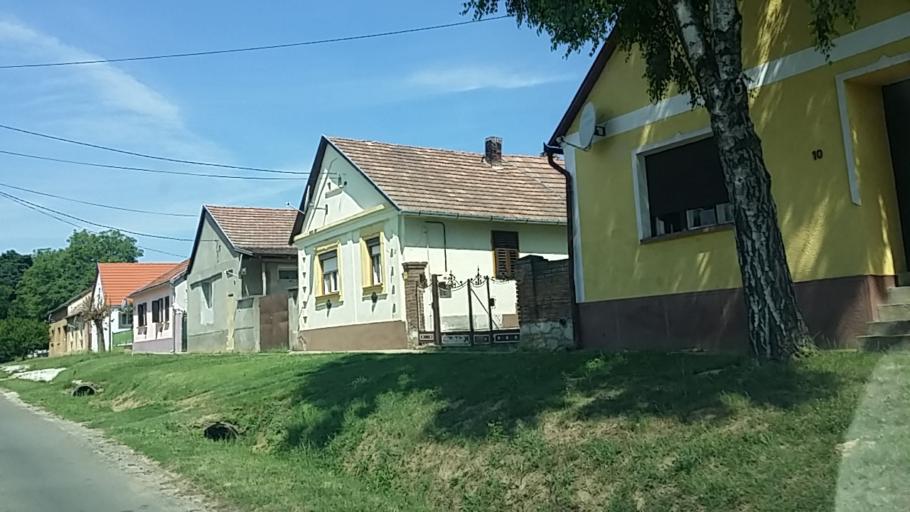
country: HU
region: Baranya
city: Harkany
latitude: 45.8776
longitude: 18.1675
